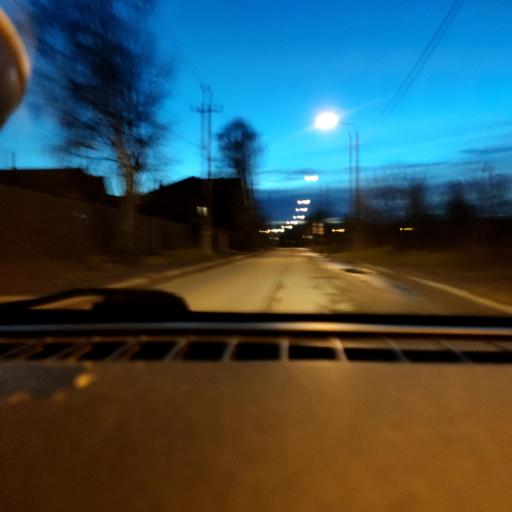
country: RU
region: Perm
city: Perm
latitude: 58.0266
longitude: 56.1769
